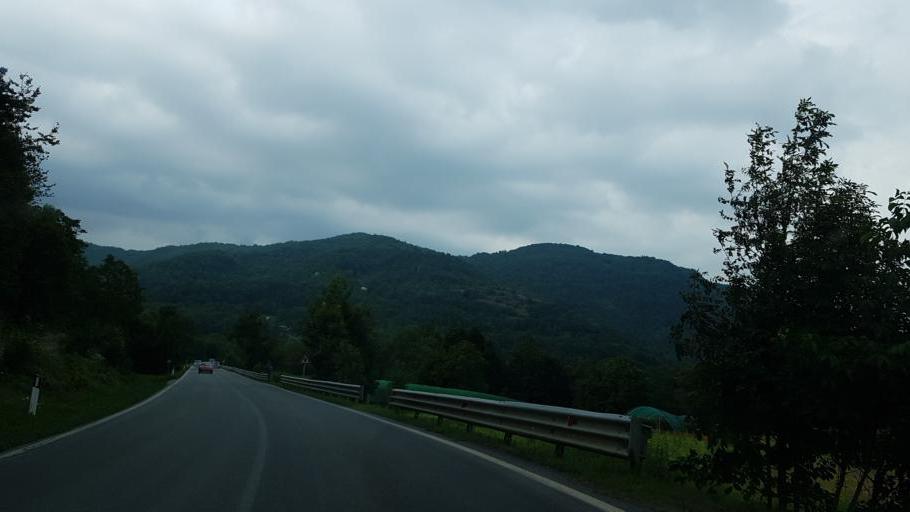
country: IT
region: Piedmont
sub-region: Provincia di Cuneo
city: Moiola
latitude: 44.3263
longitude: 7.3970
